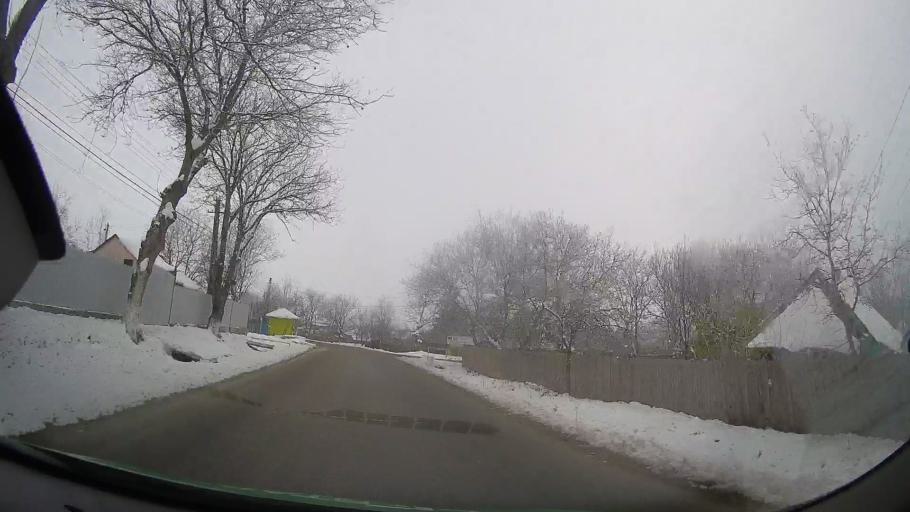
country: RO
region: Bacau
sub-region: Comuna Oncesti
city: Oncesti
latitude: 46.4520
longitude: 27.2621
